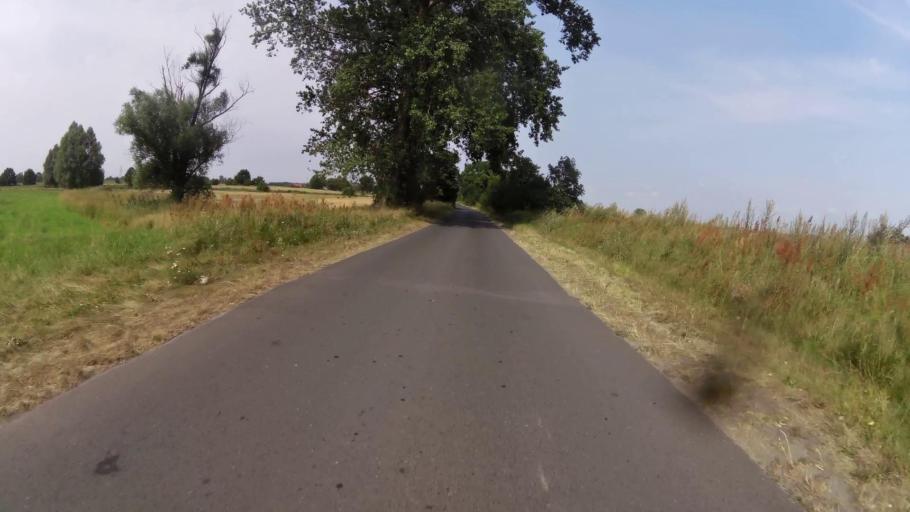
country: PL
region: West Pomeranian Voivodeship
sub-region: Powiat mysliborski
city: Nowogrodek Pomorski
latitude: 52.9689
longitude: 15.0223
